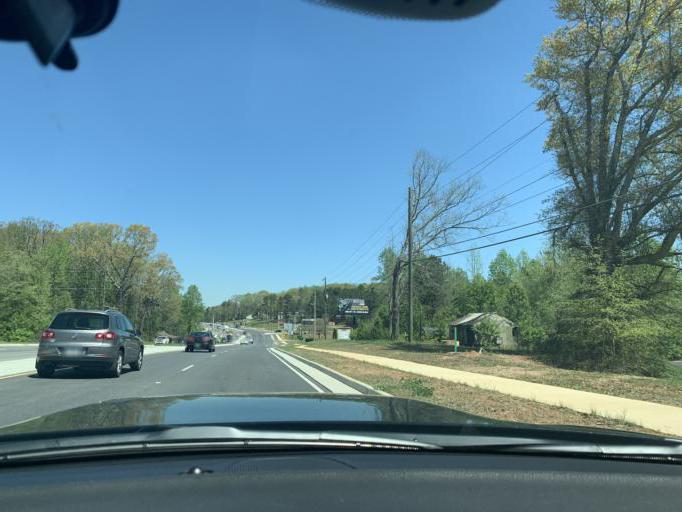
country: US
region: Georgia
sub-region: Forsyth County
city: Cumming
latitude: 34.1975
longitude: -84.1970
